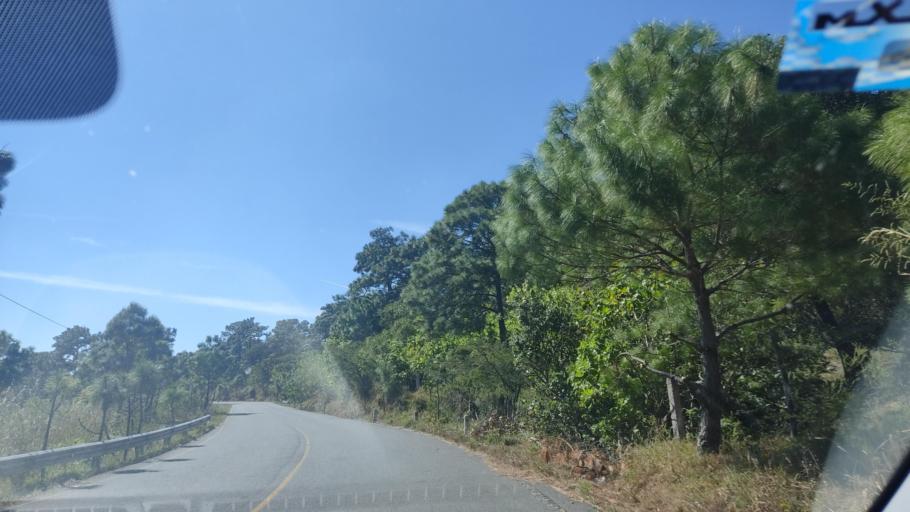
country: MX
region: Nayarit
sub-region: Jala
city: Rosa Blanca
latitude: 21.0983
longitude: -104.3783
